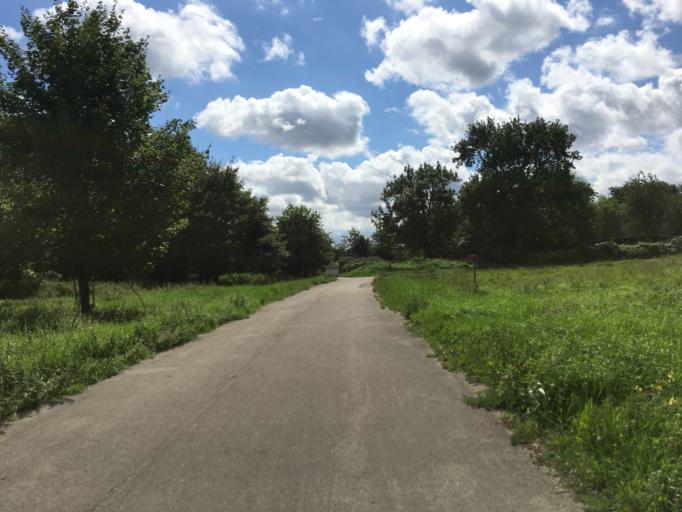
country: DE
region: North Rhine-Westphalia
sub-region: Regierungsbezirk Koln
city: Dueren
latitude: 50.7786
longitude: 6.4785
